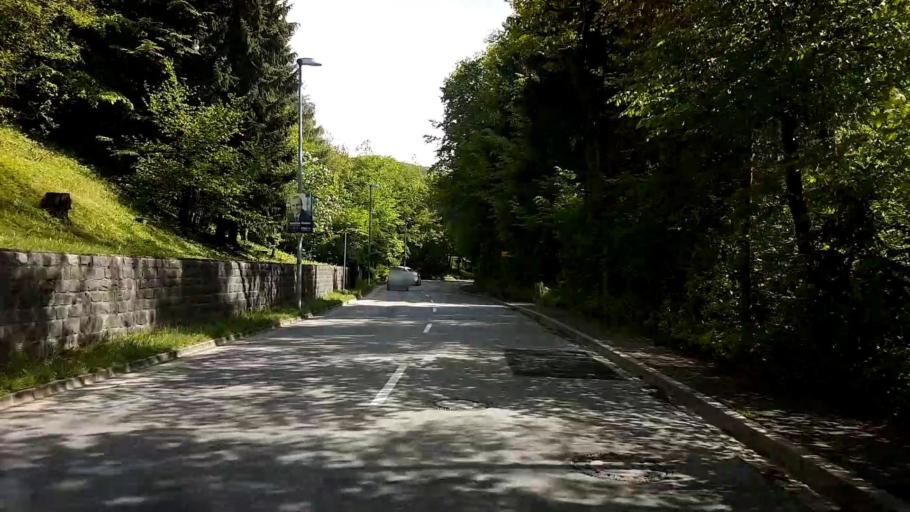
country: DE
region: Bavaria
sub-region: Upper Franconia
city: Ebermannstadt
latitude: 49.7872
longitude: 11.1804
